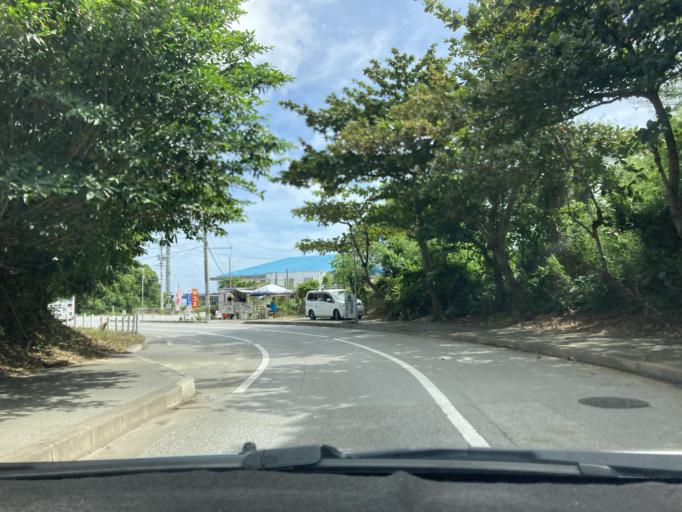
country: JP
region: Okinawa
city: Ginowan
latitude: 26.1685
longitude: 127.8274
